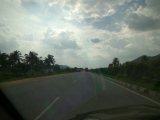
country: IN
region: Karnataka
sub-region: Kolar
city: Kolar
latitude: 13.1231
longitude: 78.0626
